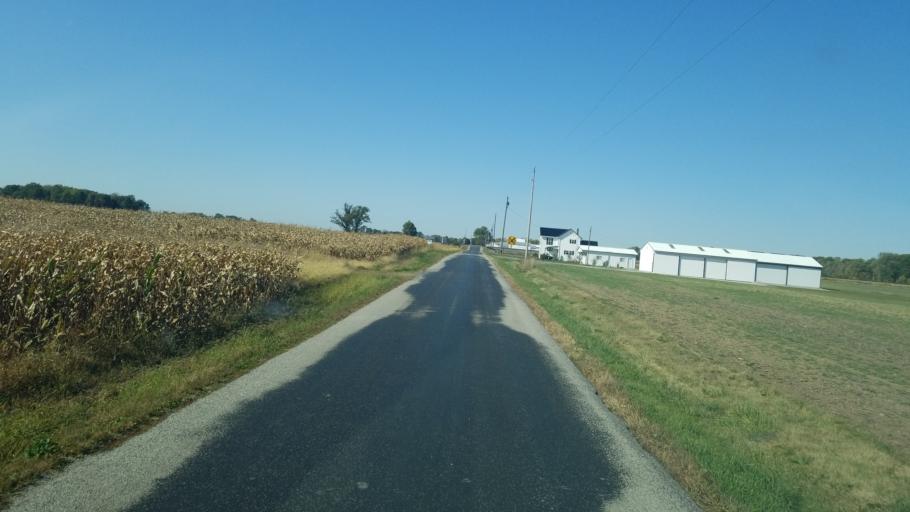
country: US
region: Ohio
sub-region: Marion County
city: Prospect
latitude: 40.4695
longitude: -83.0916
